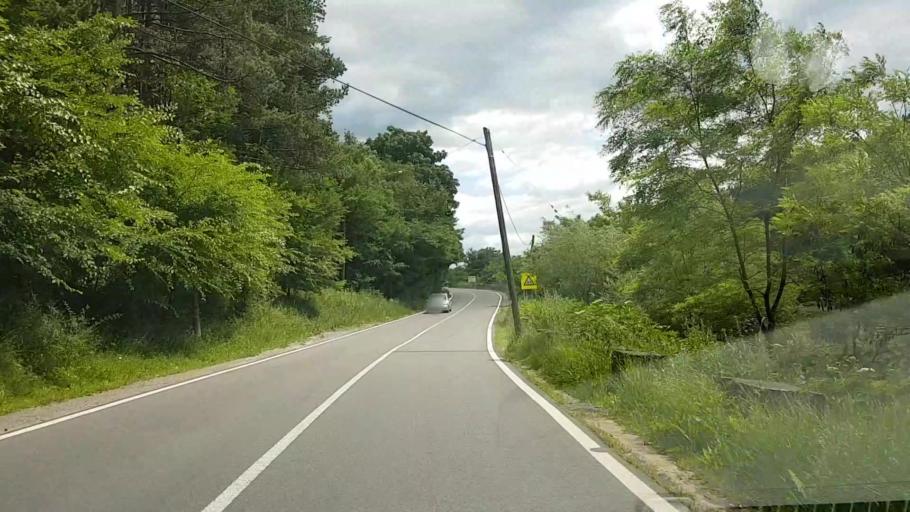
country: RO
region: Neamt
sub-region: Comuna Poiana Teiului
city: Poiana Teiului
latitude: 47.1213
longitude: 25.9104
